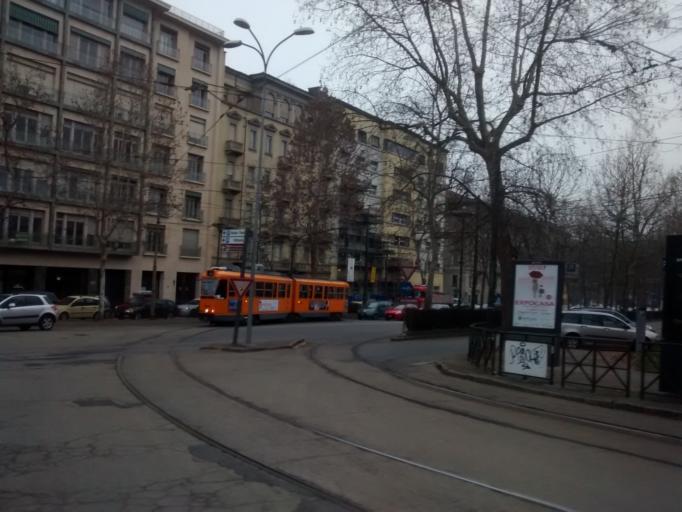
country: IT
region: Piedmont
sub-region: Provincia di Torino
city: Turin
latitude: 45.0594
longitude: 7.6880
